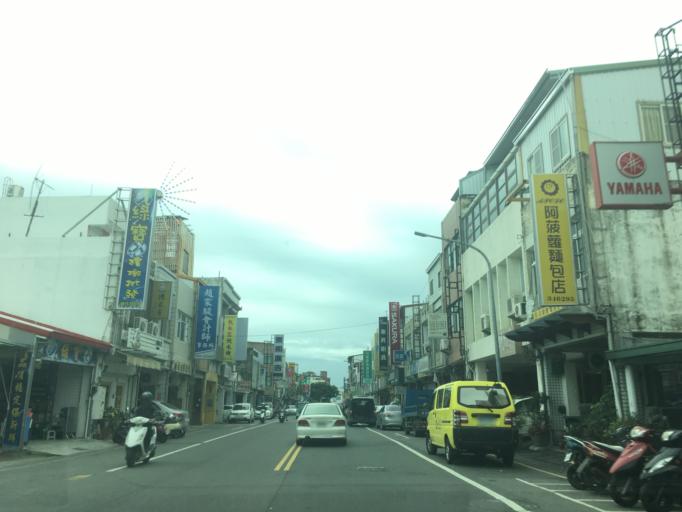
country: TW
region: Taiwan
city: Taitung City
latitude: 22.7586
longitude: 121.1411
